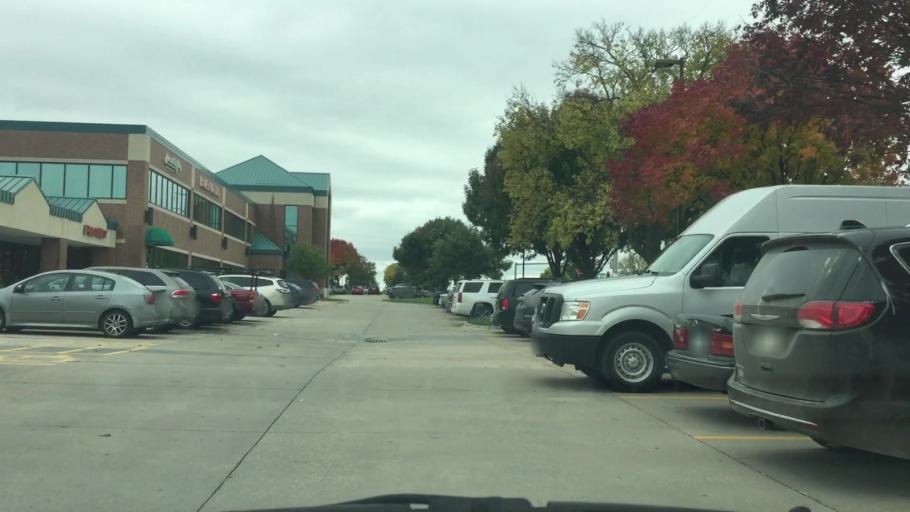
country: US
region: Iowa
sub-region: Polk County
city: Clive
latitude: 41.5971
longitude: -93.7708
